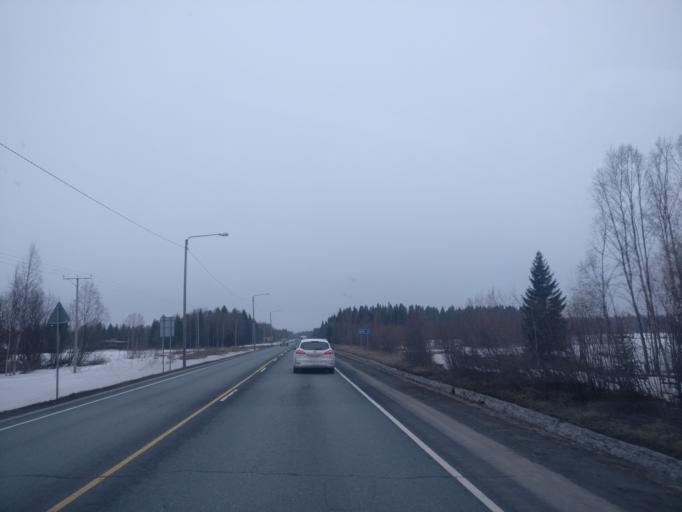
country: FI
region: Lapland
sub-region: Kemi-Tornio
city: Simo
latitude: 65.6701
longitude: 24.9244
